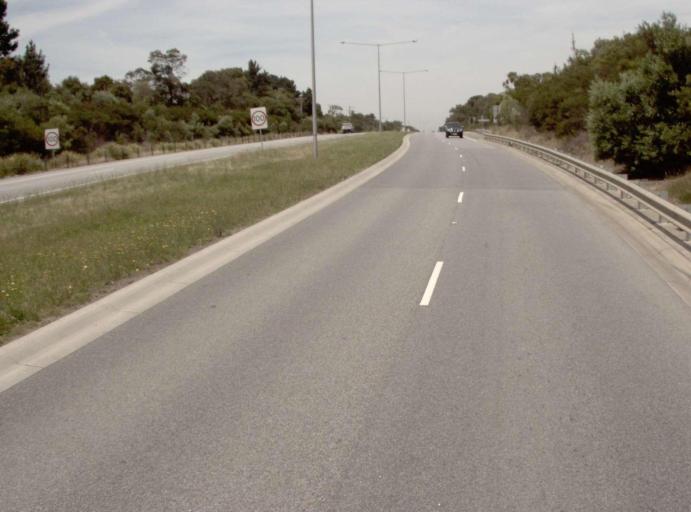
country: AU
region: Victoria
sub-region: Casey
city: Cranbourne South
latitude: -38.1439
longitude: 145.2263
